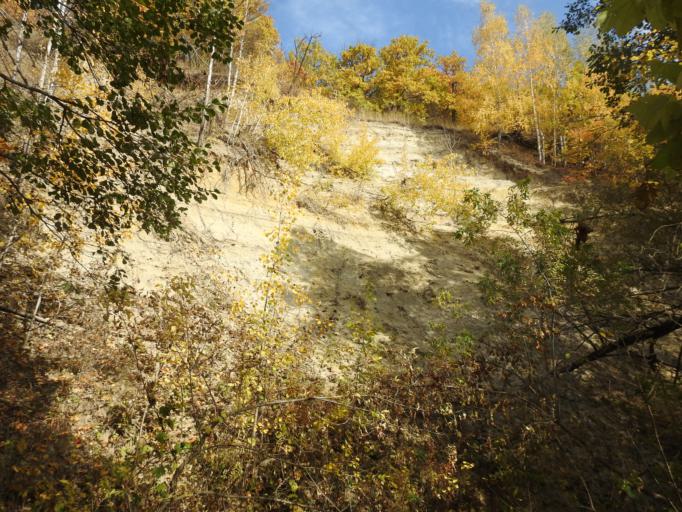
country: RU
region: Saratov
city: Baltay
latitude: 52.5240
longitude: 46.7702
